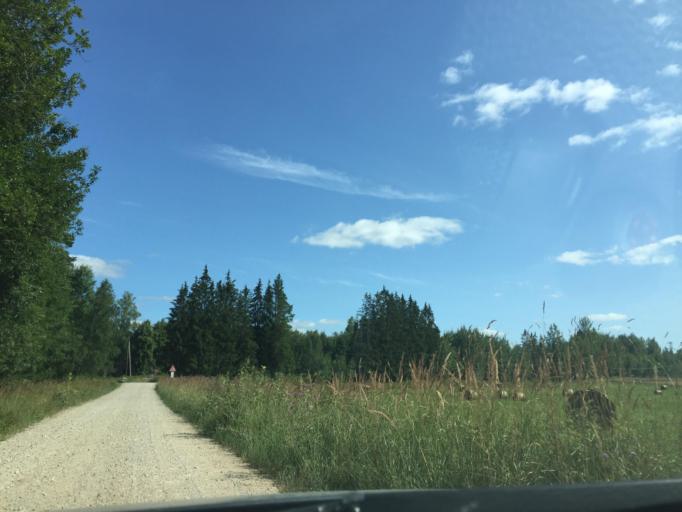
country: LV
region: Talsu Rajons
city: Stende
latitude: 57.1866
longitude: 22.3237
